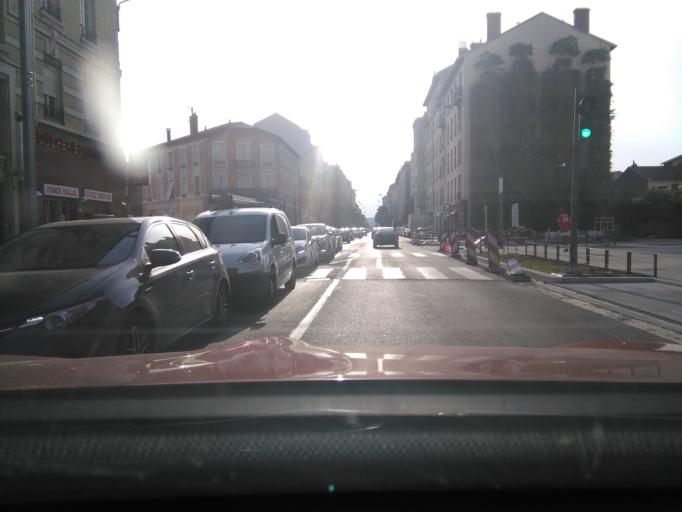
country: FR
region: Rhone-Alpes
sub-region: Departement du Rhone
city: Villeurbanne
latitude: 45.7660
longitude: 4.8984
